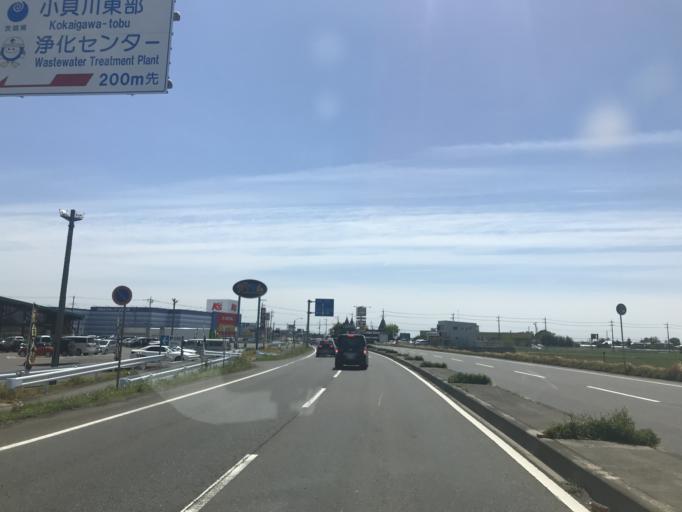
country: JP
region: Ibaraki
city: Ishige
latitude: 36.2006
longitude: 139.9843
